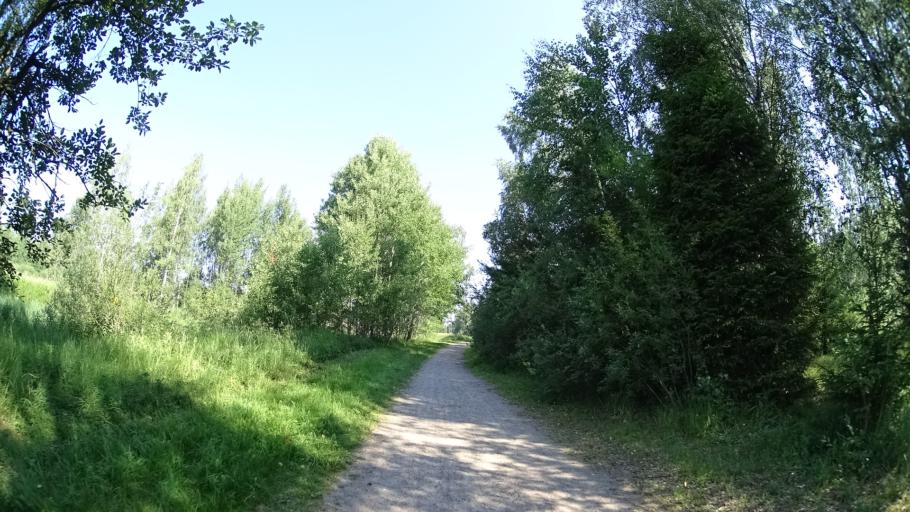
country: FI
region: Uusimaa
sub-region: Helsinki
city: Kerava
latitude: 60.3514
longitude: 25.1261
